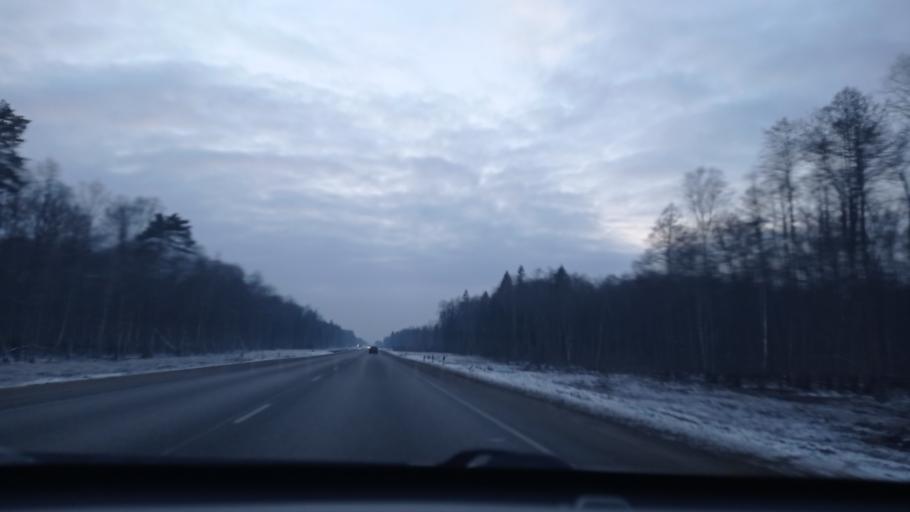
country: RU
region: Kaluga
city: Belousovo
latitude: 55.1268
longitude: 36.7534
